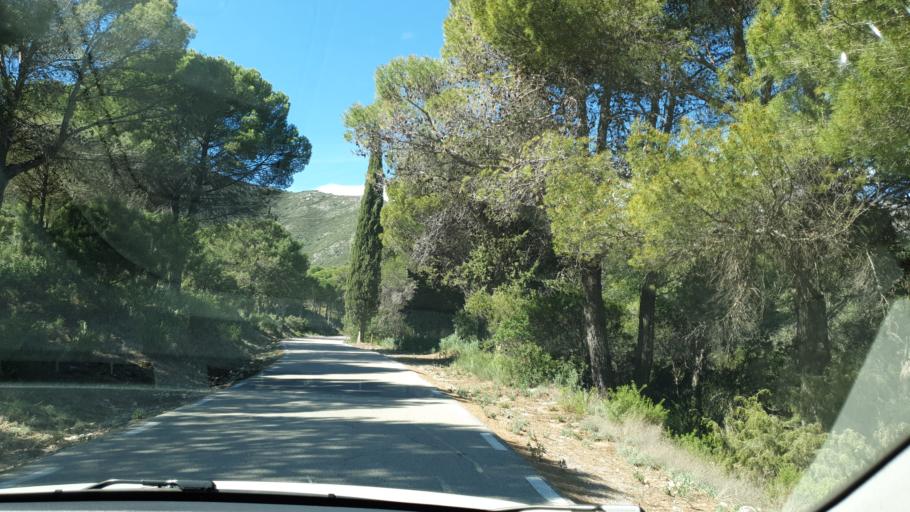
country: ES
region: Andalusia
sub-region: Provincia de Malaga
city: Ojen
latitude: 36.5878
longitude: -4.8634
